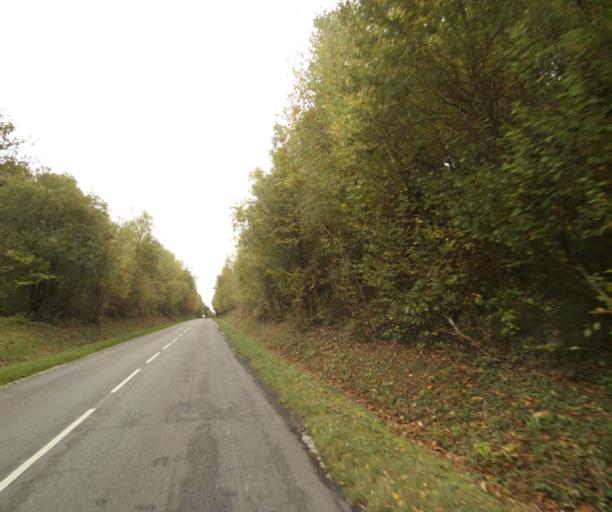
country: FR
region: Centre
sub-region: Departement d'Eure-et-Loir
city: Dreux
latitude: 48.7690
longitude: 1.3701
